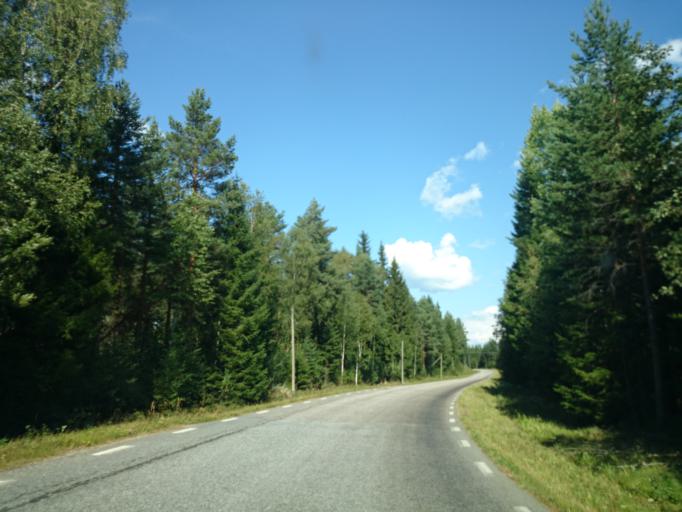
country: SE
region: Gaevleborg
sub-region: Ljusdals Kommun
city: Jaervsoe
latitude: 61.7609
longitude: 16.2049
